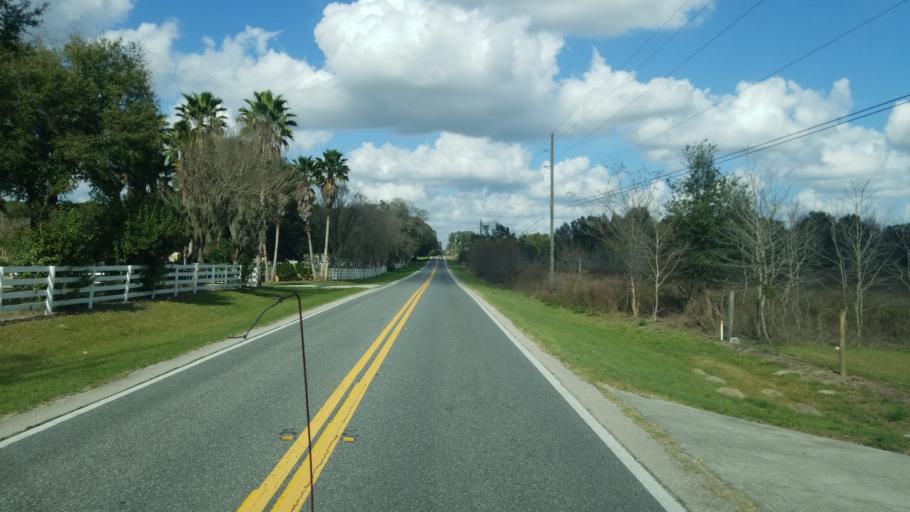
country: US
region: Florida
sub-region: Marion County
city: Belleview
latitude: 28.9905
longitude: -82.1199
